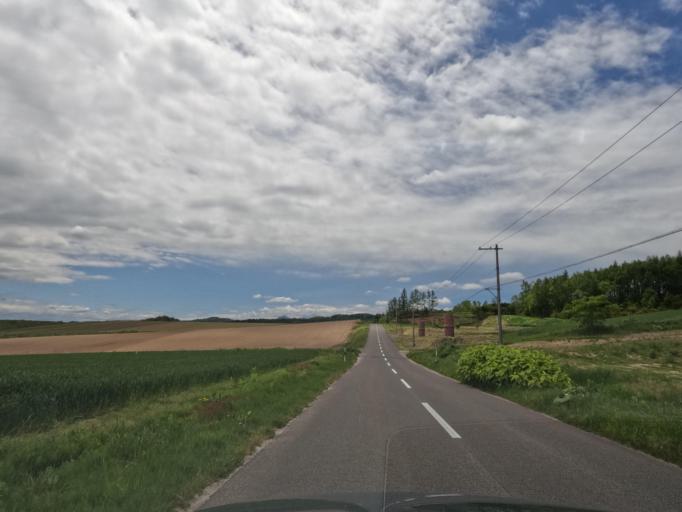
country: JP
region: Hokkaido
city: Shimo-furano
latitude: 43.5047
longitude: 142.4165
